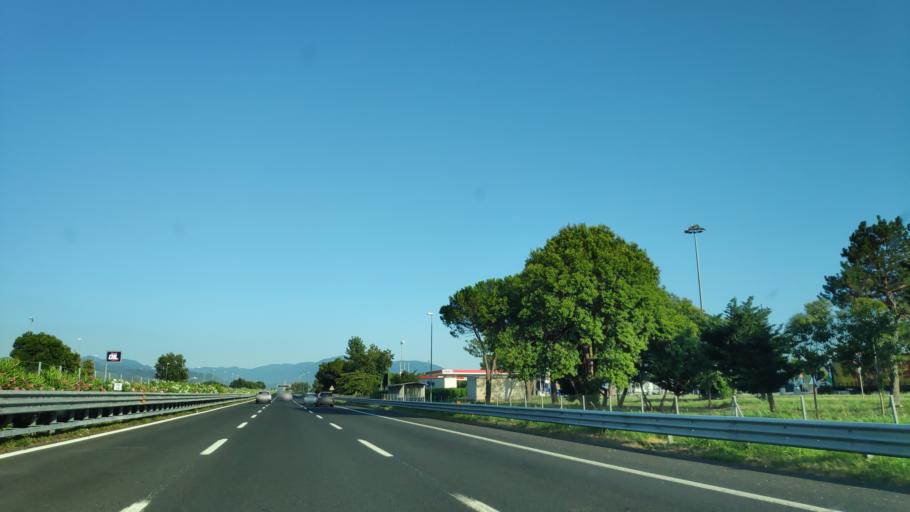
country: IT
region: Campania
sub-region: Provincia di Napoli
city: San Vitaliano
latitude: 40.9523
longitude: 14.4690
